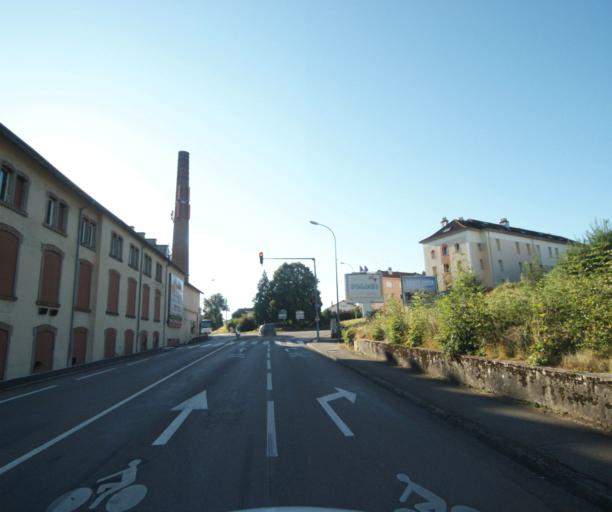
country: FR
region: Lorraine
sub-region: Departement des Vosges
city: Chantraine
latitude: 48.1504
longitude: 6.4545
